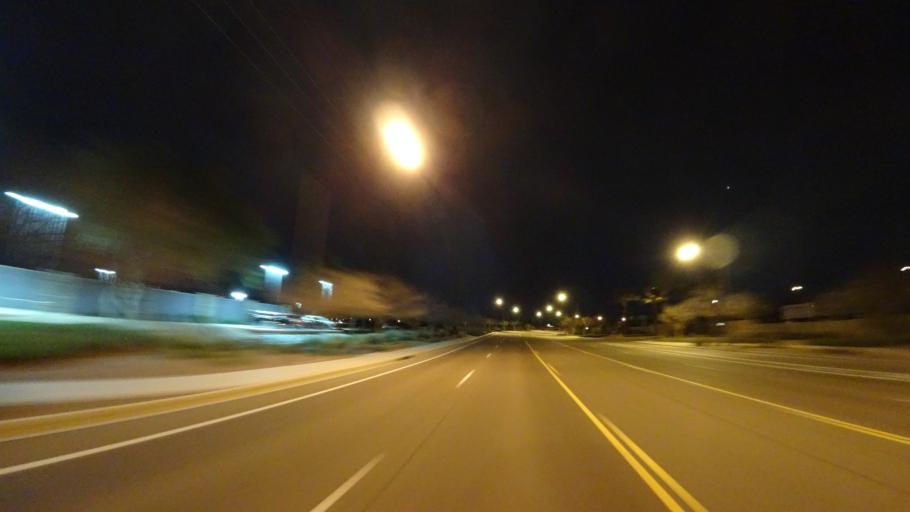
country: US
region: Arizona
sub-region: Maricopa County
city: Gilbert
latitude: 33.2935
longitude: -111.7610
